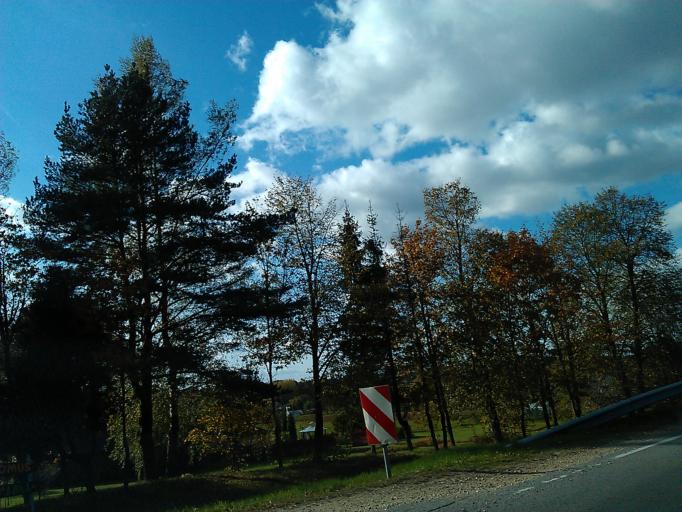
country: LV
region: Jekabpils Rajons
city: Jekabpils
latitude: 56.4780
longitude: 25.9325
